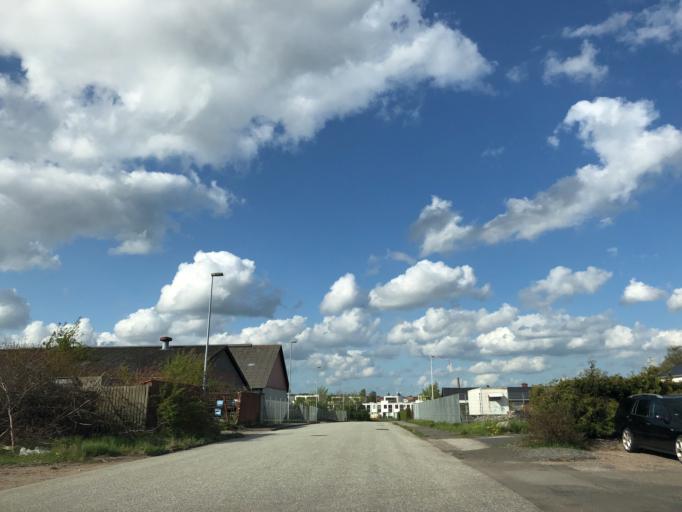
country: DK
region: Zealand
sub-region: Ringsted Kommune
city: Ringsted
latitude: 55.4331
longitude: 11.7936
